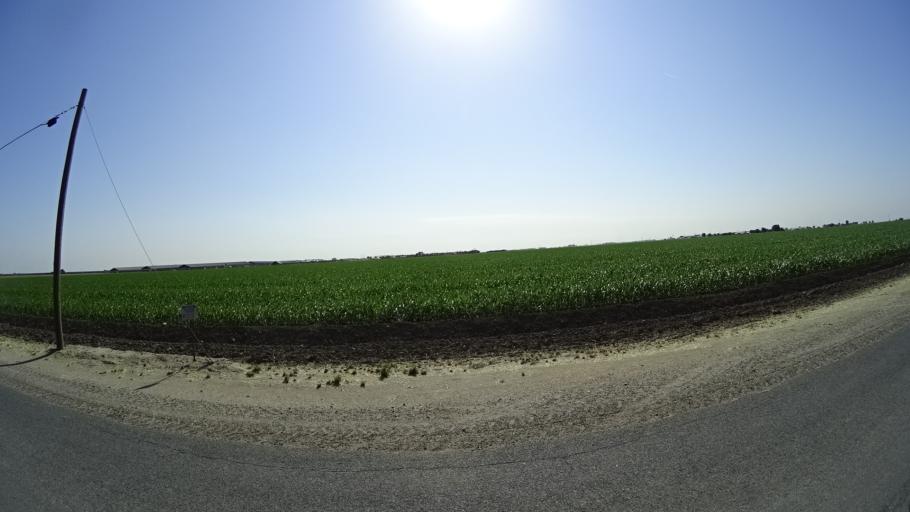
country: US
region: California
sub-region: Kings County
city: Home Garden
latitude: 36.2455
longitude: -119.5831
